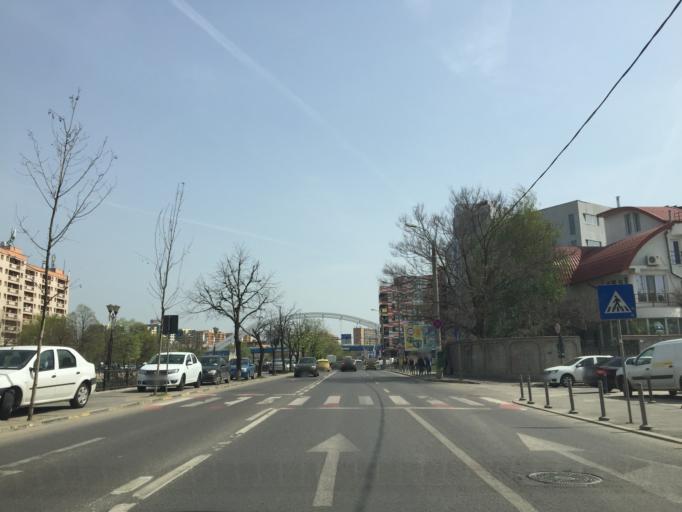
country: RO
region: Bucuresti
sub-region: Municipiul Bucuresti
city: Bucuresti
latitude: 44.4436
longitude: 26.0566
